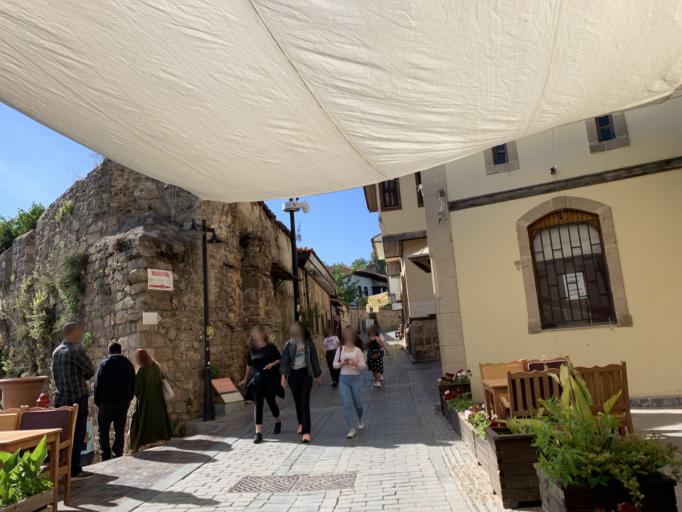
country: TR
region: Antalya
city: Antalya
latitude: 36.8848
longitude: 30.7040
